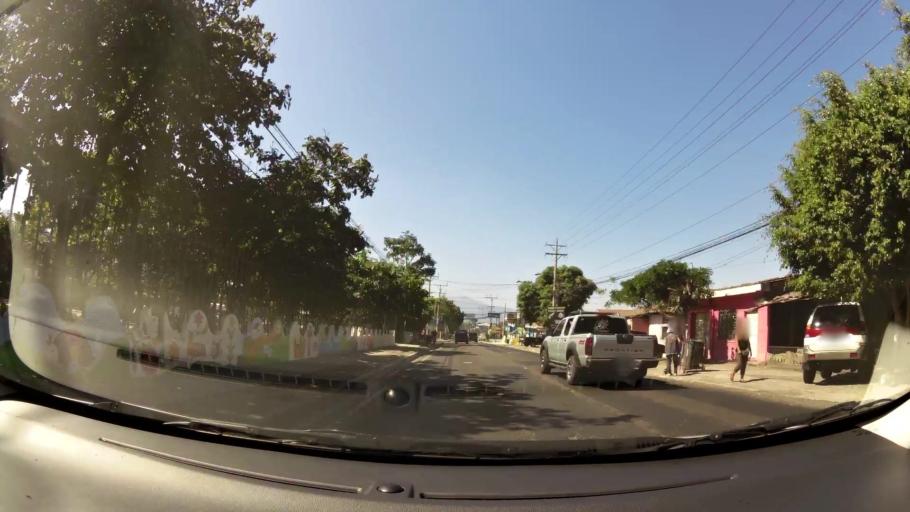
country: SV
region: La Libertad
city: Santa Tecla
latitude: 13.7221
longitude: -89.3661
